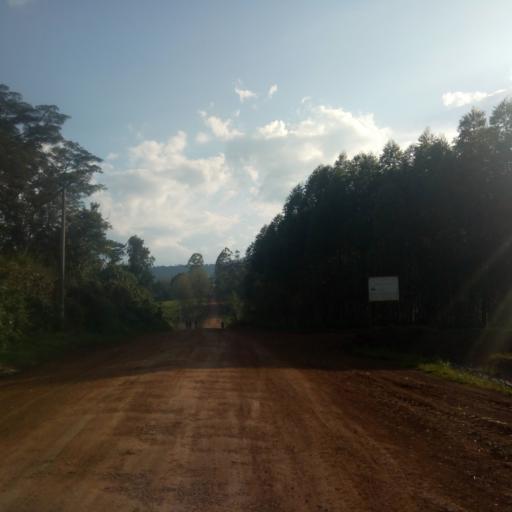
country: ET
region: Oromiya
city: Gore
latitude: 7.8416
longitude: 35.4754
